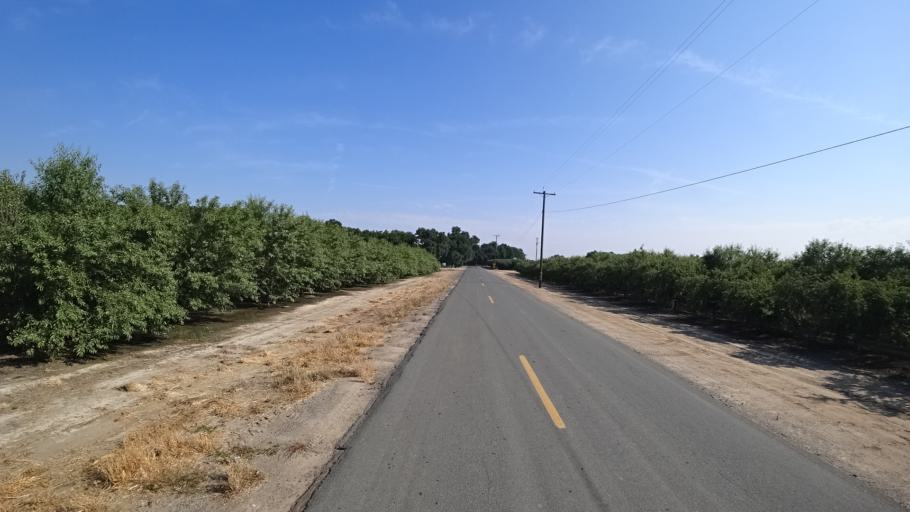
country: US
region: California
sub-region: Kings County
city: Lemoore
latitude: 36.3341
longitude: -119.8347
